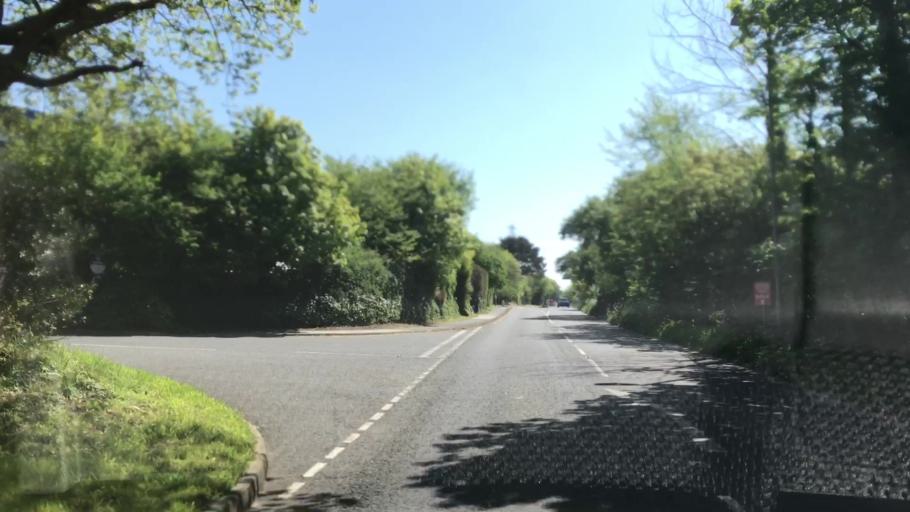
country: GB
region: England
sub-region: Cornwall
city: Chacewater
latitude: 50.2641
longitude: -5.1265
